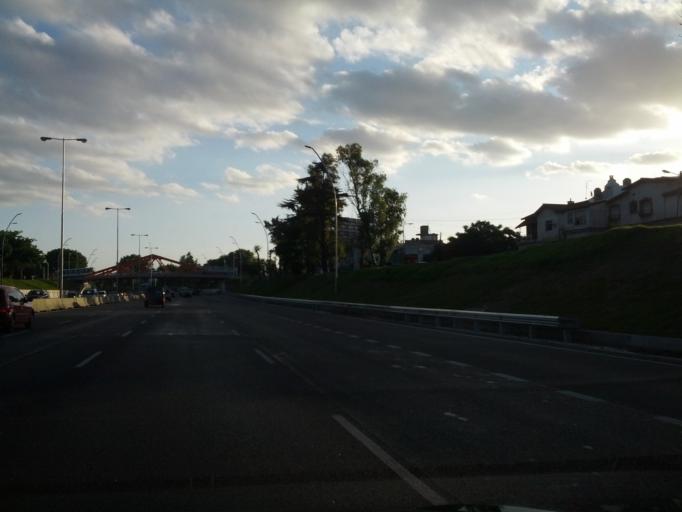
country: AR
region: Buenos Aires
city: Caseros
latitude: -34.6131
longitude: -58.5299
